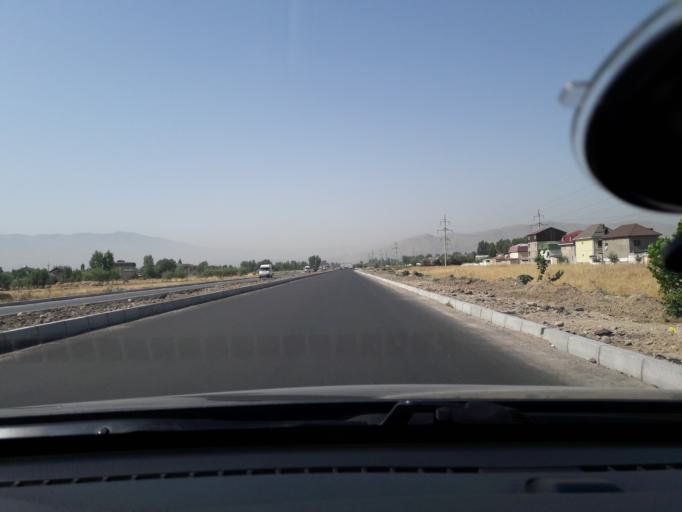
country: TJ
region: Dushanbe
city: Dushanbe
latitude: 38.4938
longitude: 68.7530
